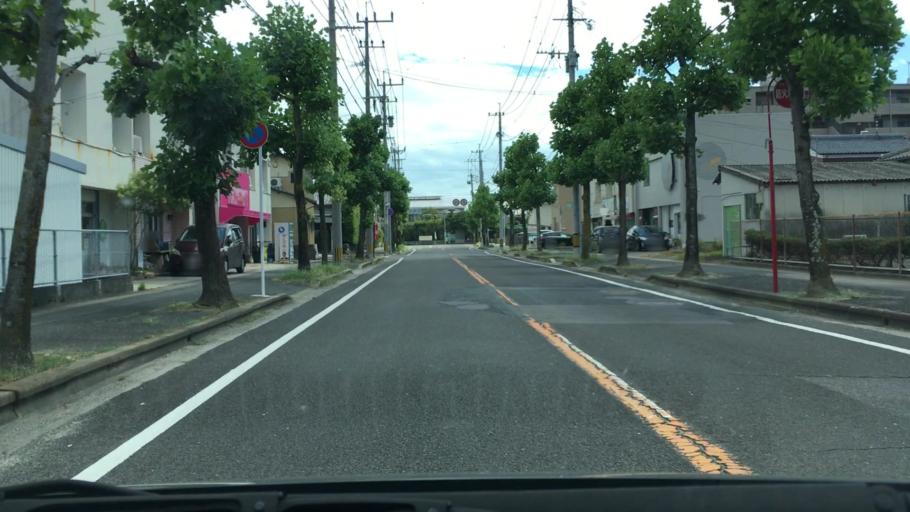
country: JP
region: Saga Prefecture
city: Saga-shi
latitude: 33.2673
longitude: 130.2872
